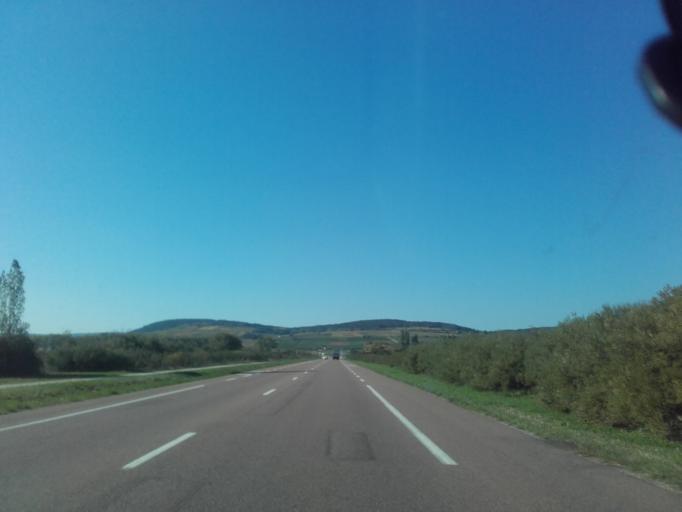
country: FR
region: Bourgogne
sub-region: Departement de la Cote-d'Or
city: Bligny-les-Beaune
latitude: 47.0081
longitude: 4.8217
